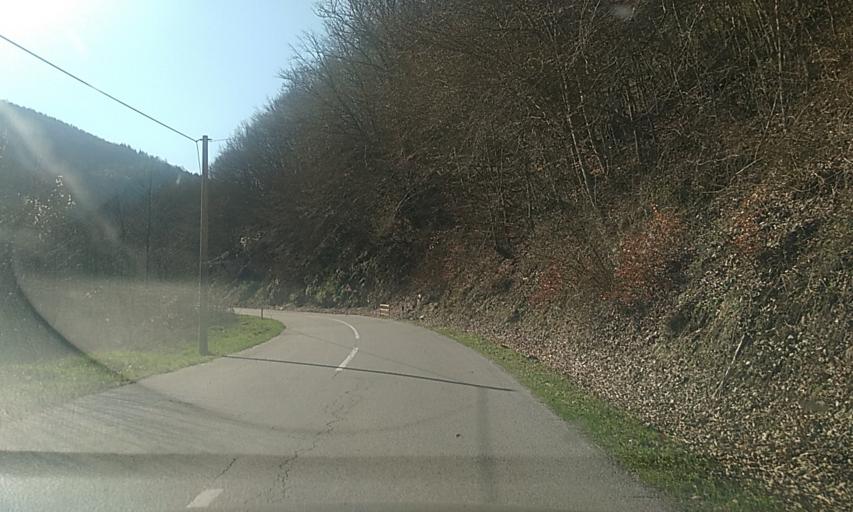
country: RS
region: Central Serbia
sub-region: Pcinjski Okrug
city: Bosilegrad
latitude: 42.4284
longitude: 22.5183
